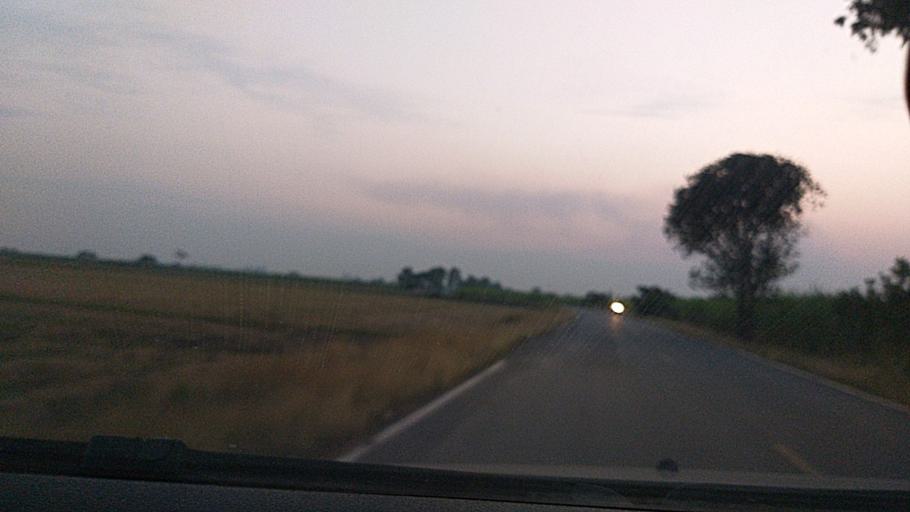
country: TH
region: Sing Buri
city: Phrom Buri
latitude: 14.8225
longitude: 100.4056
